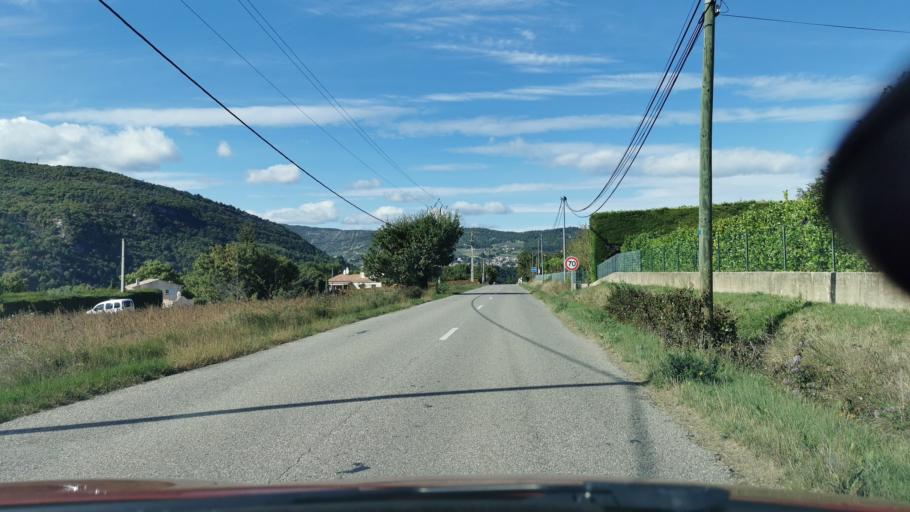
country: FR
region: Provence-Alpes-Cote d'Azur
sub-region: Departement des Alpes-de-Haute-Provence
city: Sisteron
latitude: 44.1662
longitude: 5.9600
